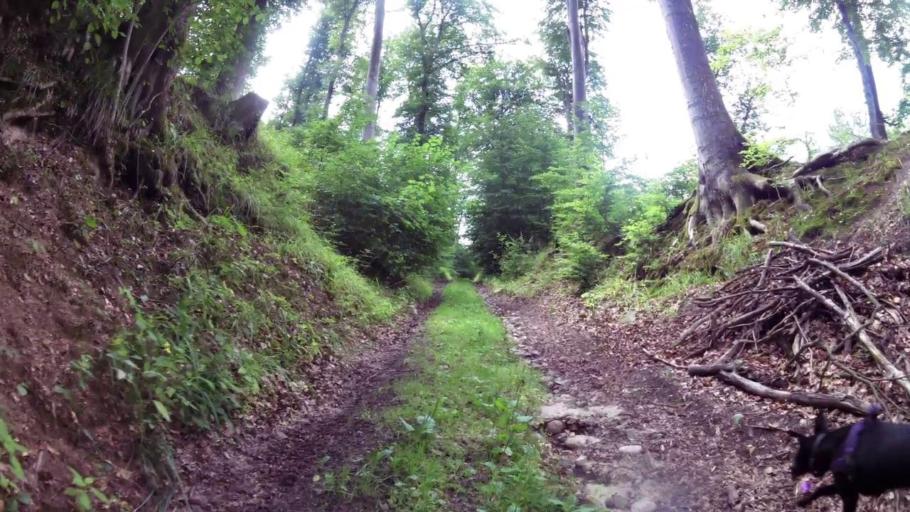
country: PL
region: West Pomeranian Voivodeship
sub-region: Powiat drawski
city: Drawsko Pomorskie
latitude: 53.5065
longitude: 15.6967
